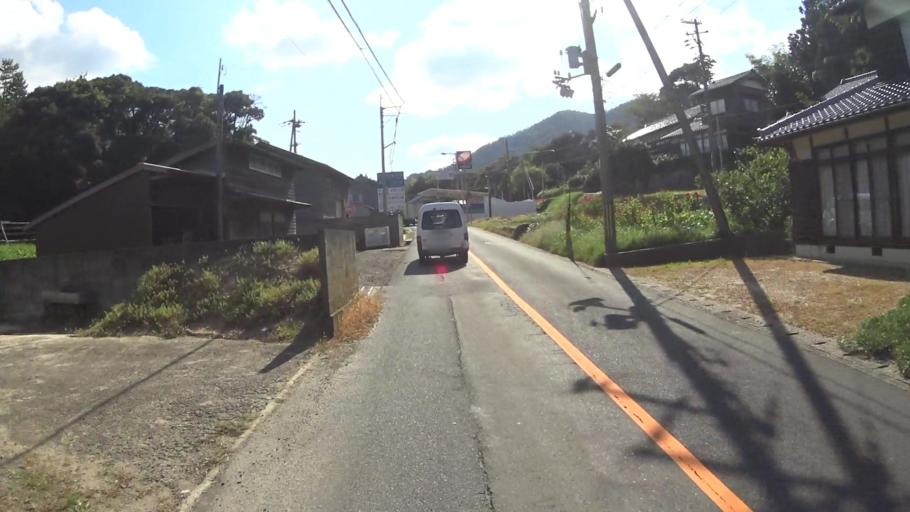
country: JP
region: Kyoto
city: Miyazu
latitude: 35.7517
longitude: 135.1681
